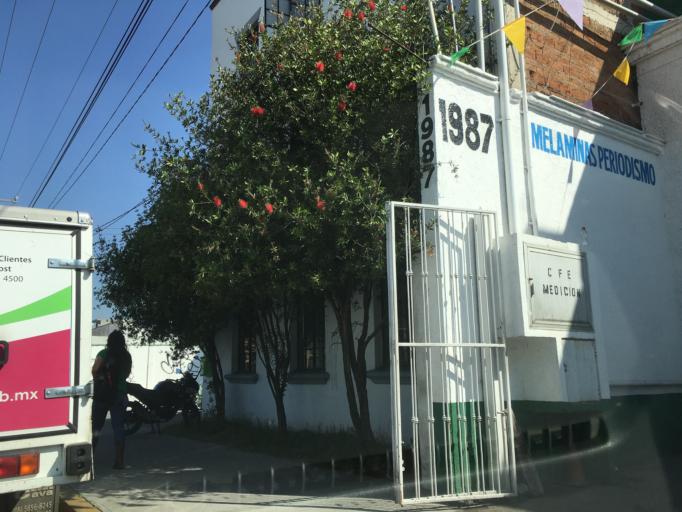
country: MX
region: Michoacan
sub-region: Morelia
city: Morelos
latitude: 19.6823
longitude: -101.2257
